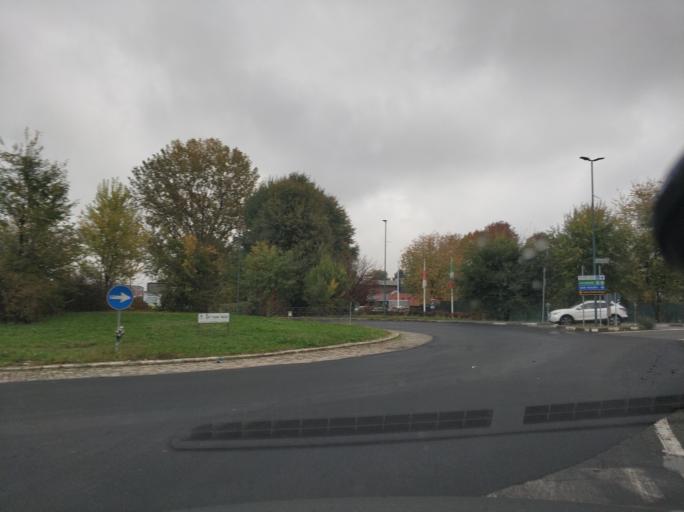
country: IT
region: Piedmont
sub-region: Provincia di Torino
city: Settimo Torinese
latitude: 45.1260
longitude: 7.7505
